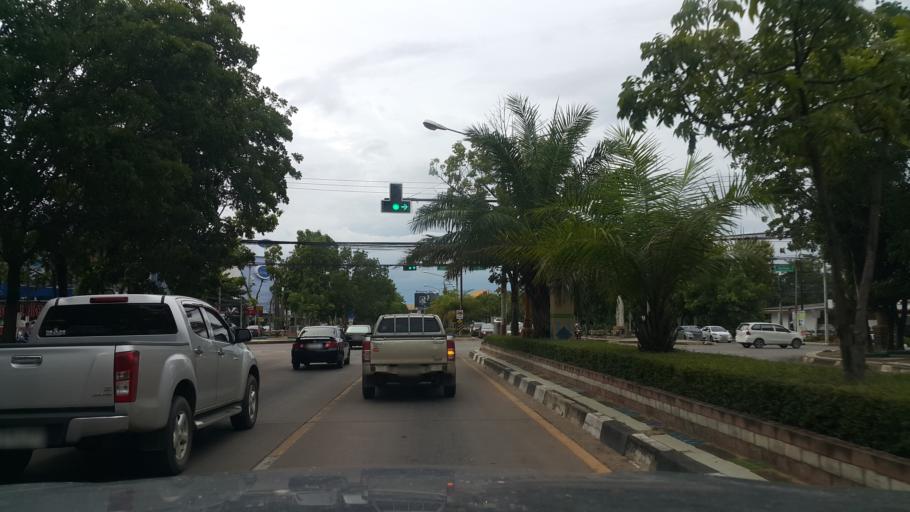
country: TH
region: Lampang
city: Lampang
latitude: 18.2816
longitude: 99.4877
